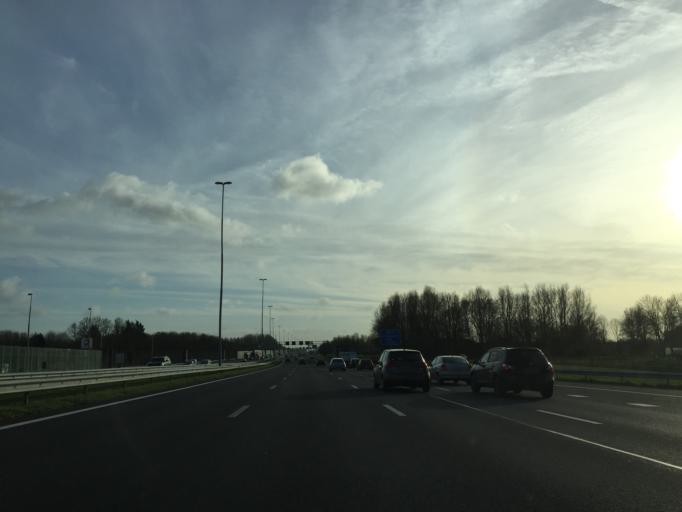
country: NL
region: Utrecht
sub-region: Gemeente Nieuwegein
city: Nieuwegein
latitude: 52.0170
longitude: 5.0674
